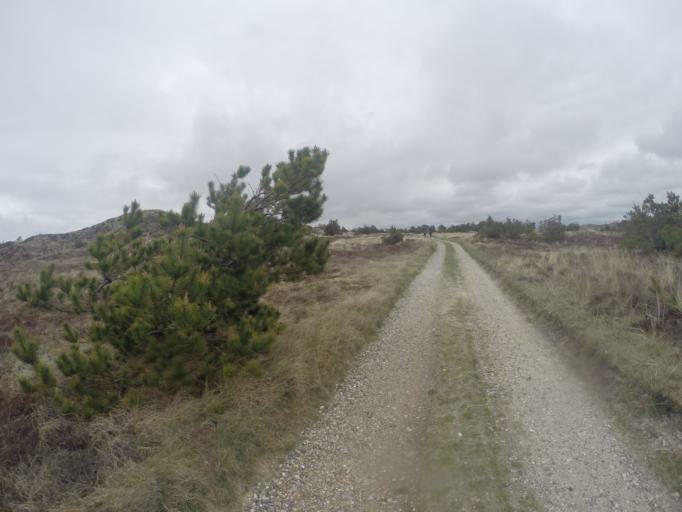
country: DK
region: North Denmark
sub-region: Thisted Kommune
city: Hurup
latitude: 56.8792
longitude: 8.3153
